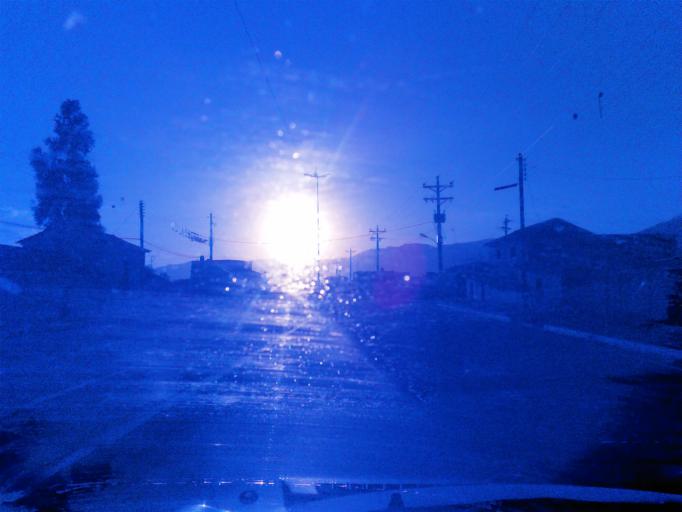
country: BO
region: Cochabamba
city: Punata
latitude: -17.5498
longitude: -65.8234
